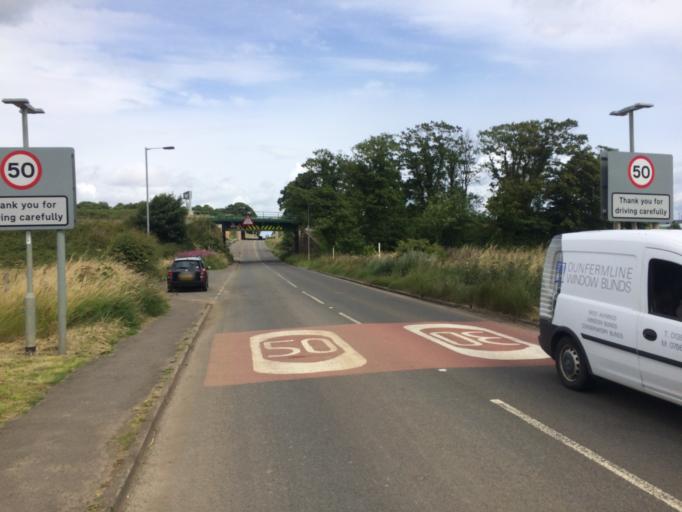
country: GB
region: Scotland
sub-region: Edinburgh
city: Kirkliston
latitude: 55.9621
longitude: -3.4035
